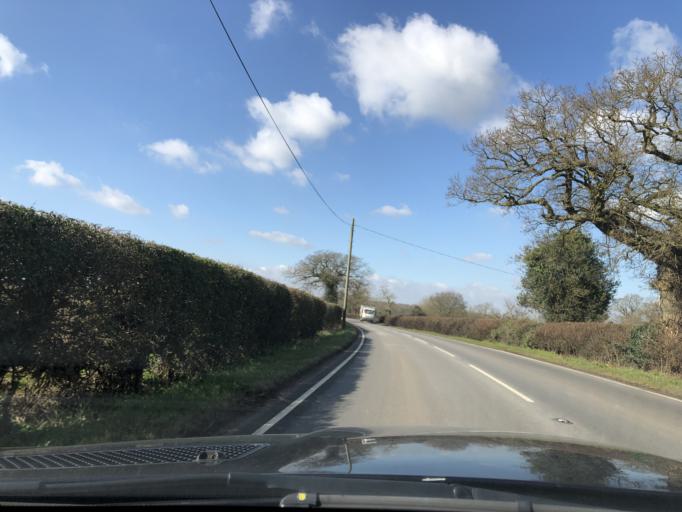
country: GB
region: England
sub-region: Warwickshire
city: Wolston
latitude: 52.3372
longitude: -1.3764
